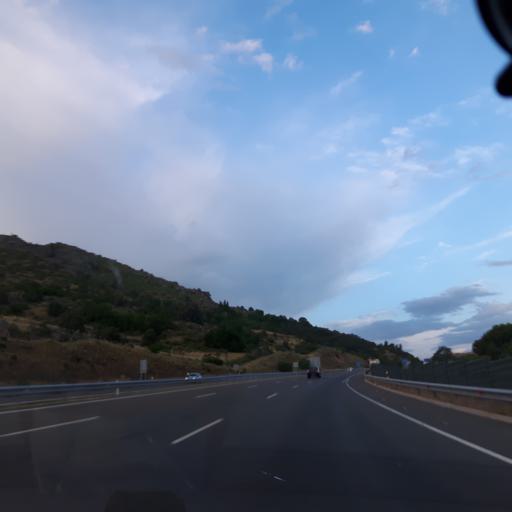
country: ES
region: Castille and Leon
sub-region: Provincia de Salamanca
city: Fresnedoso
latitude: 40.4308
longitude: -5.6962
